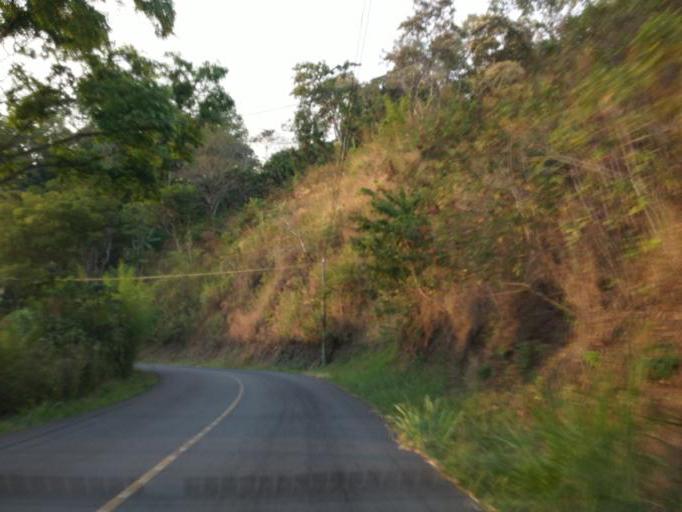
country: CR
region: San Jose
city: Palmichal
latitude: 9.8320
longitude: -84.2036
